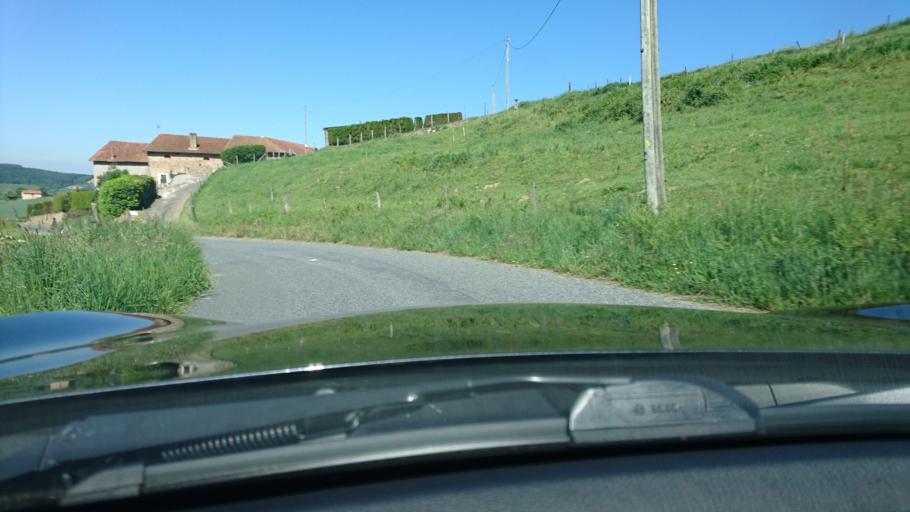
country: FR
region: Rhone-Alpes
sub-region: Departement de la Loire
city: Violay
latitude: 45.8281
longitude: 4.3890
